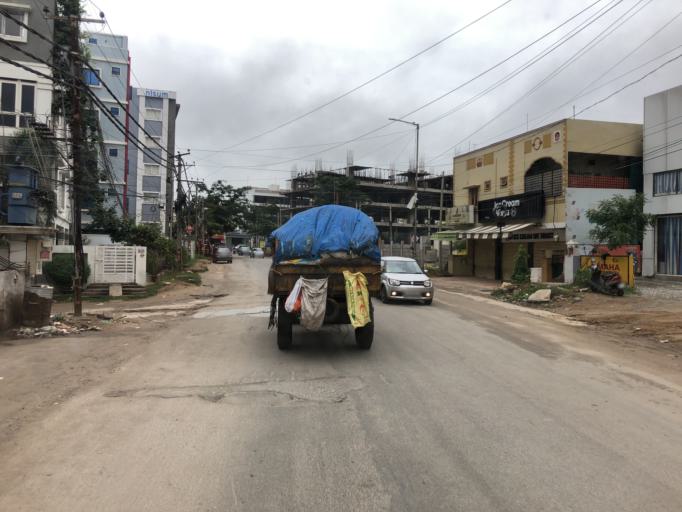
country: IN
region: Telangana
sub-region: Rangareddi
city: Kukatpalli
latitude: 17.4644
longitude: 78.3686
